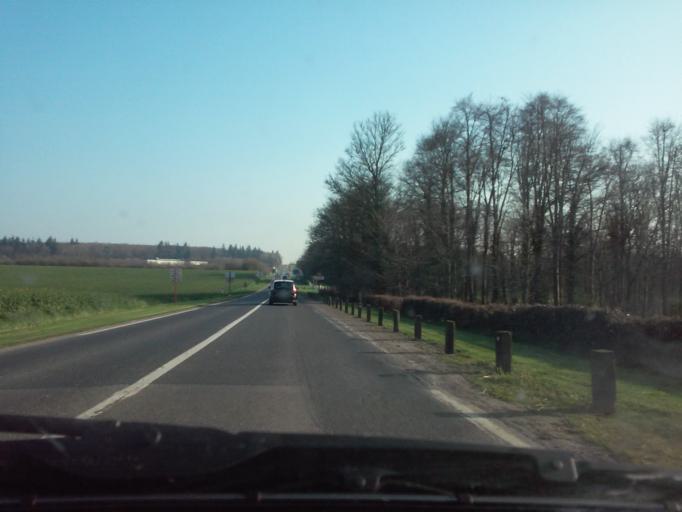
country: FR
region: Lower Normandy
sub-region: Departement du Calvados
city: Villers-Bocage
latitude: 49.0725
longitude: -0.6591
